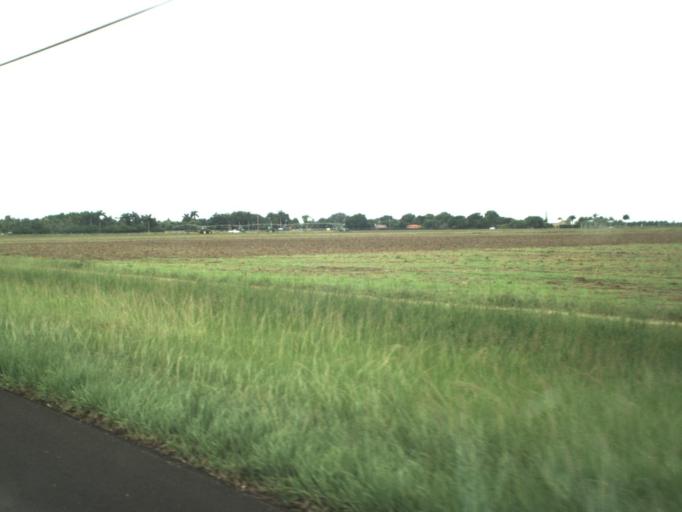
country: US
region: Florida
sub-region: Miami-Dade County
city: Richmond West
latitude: 25.6142
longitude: -80.4792
